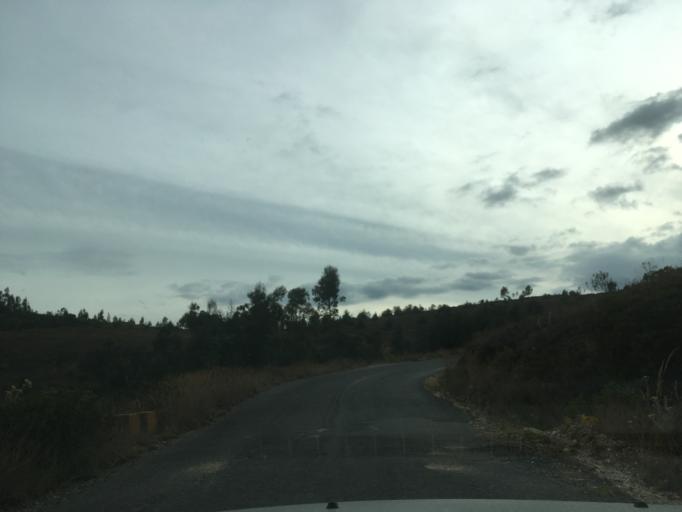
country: CO
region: Boyaca
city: Firavitoba
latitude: 5.6738
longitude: -73.0123
